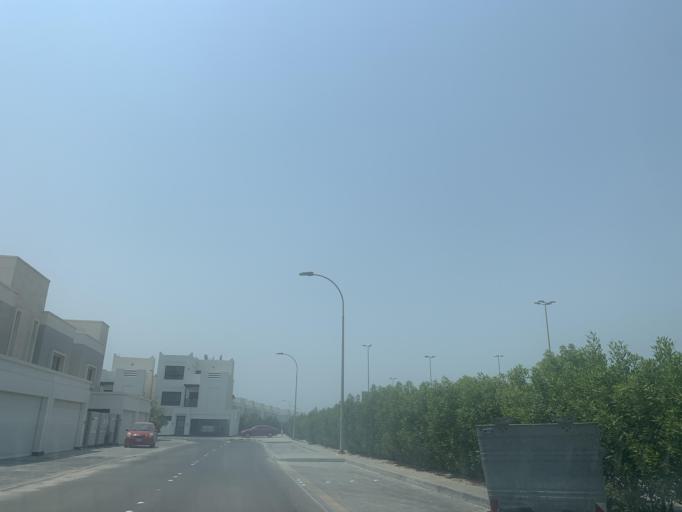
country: BH
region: Muharraq
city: Al Muharraq
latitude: 26.3107
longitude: 50.6293
